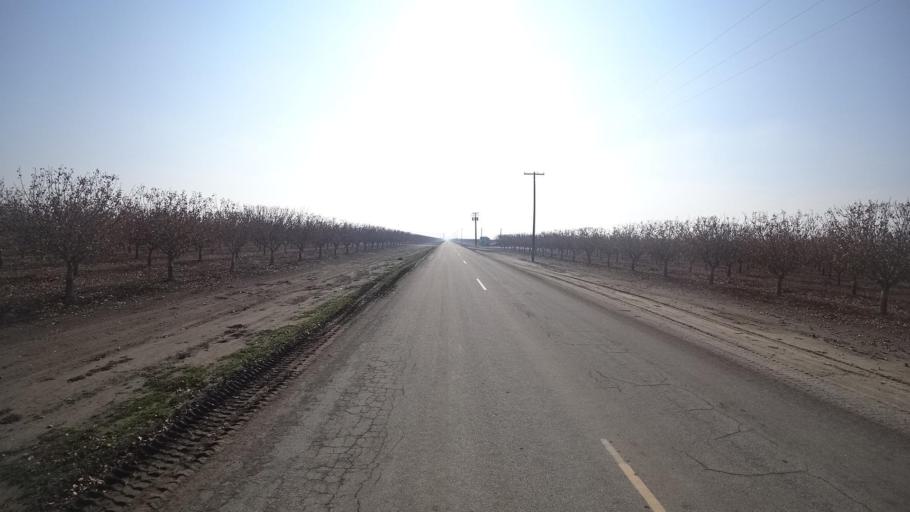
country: US
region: California
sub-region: Kern County
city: Buttonwillow
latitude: 35.3520
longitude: -119.3945
